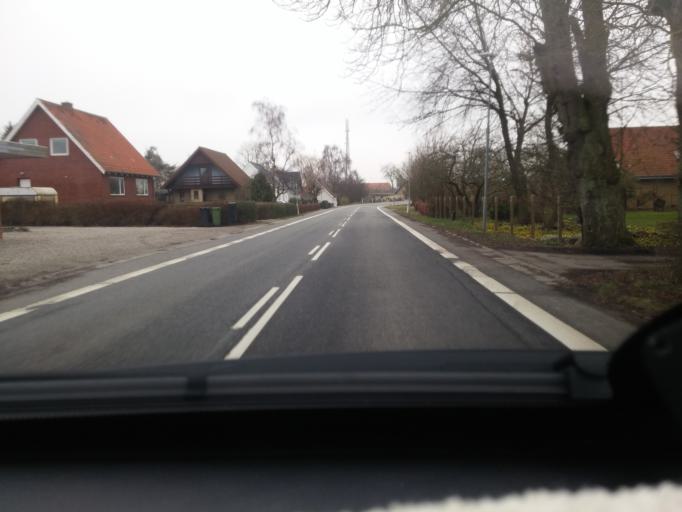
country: DK
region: South Denmark
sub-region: Nyborg Kommune
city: Ullerslev
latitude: 55.3868
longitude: 10.7239
